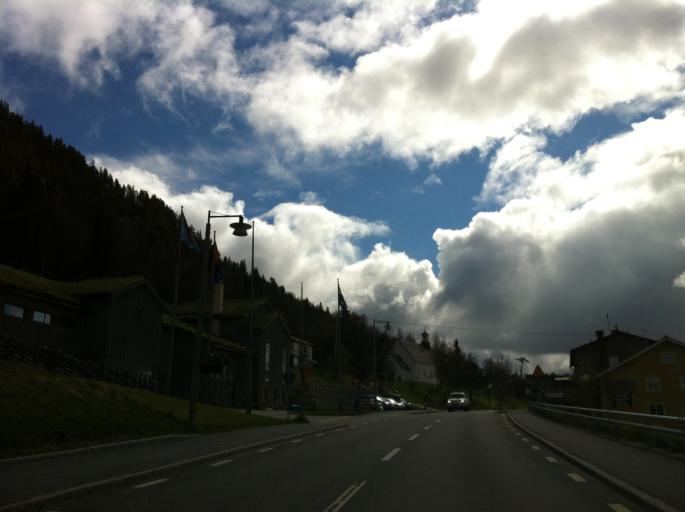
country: NO
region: Hedmark
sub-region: Engerdal
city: Engerdal
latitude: 62.5491
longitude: 12.5299
